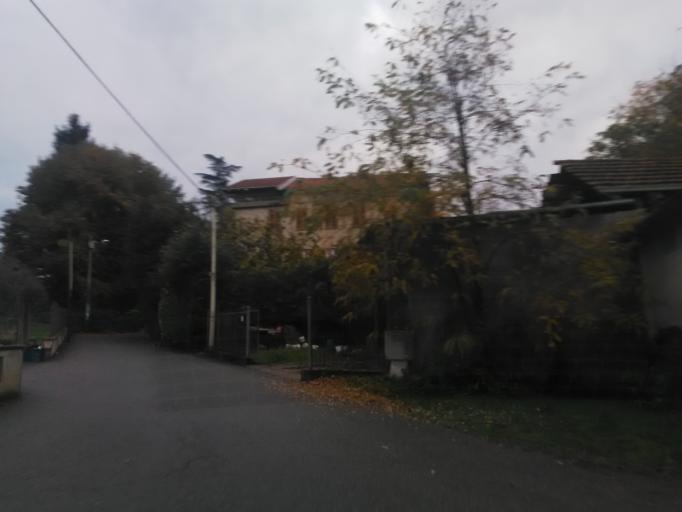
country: IT
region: Piedmont
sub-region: Provincia di Vercelli
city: Serravalle Sesia
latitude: 45.6871
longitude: 8.3154
